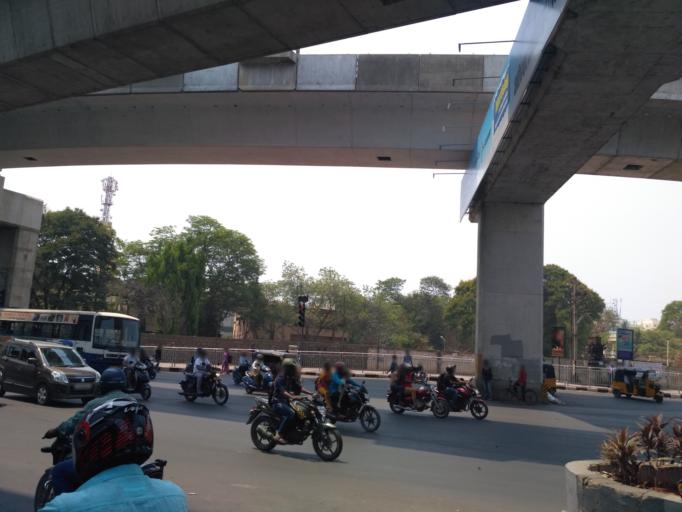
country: IN
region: Telangana
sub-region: Hyderabad
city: Hyderabad
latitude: 17.4371
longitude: 78.4439
